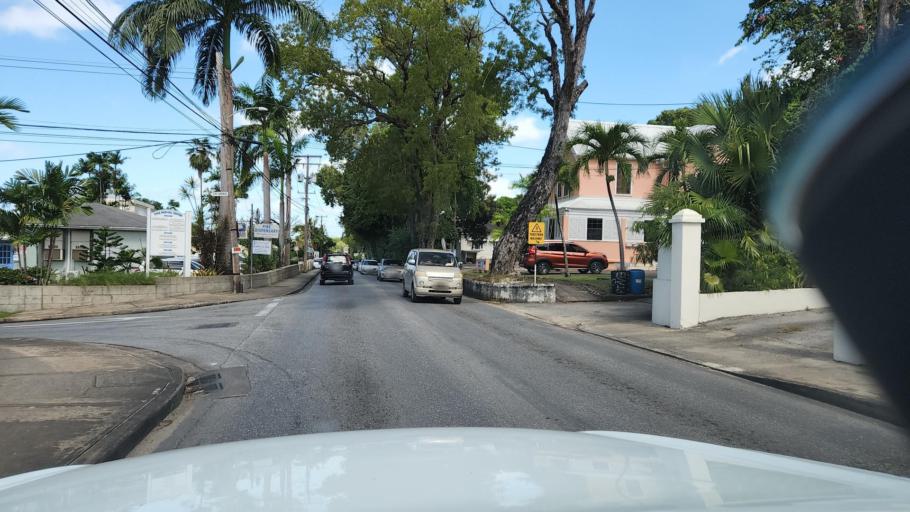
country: BB
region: Saint Michael
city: Bridgetown
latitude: 13.0945
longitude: -59.6017
